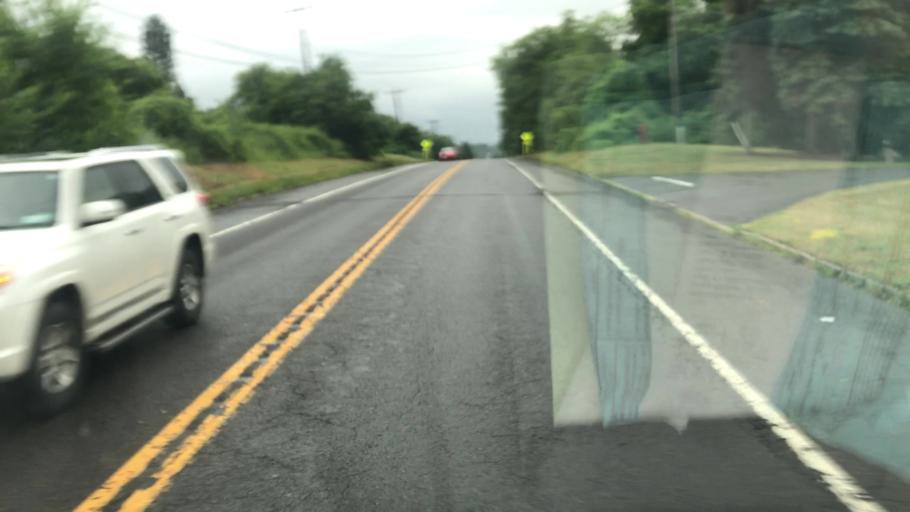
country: US
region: New York
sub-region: Onondaga County
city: Fayetteville
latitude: 43.0265
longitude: -76.0412
